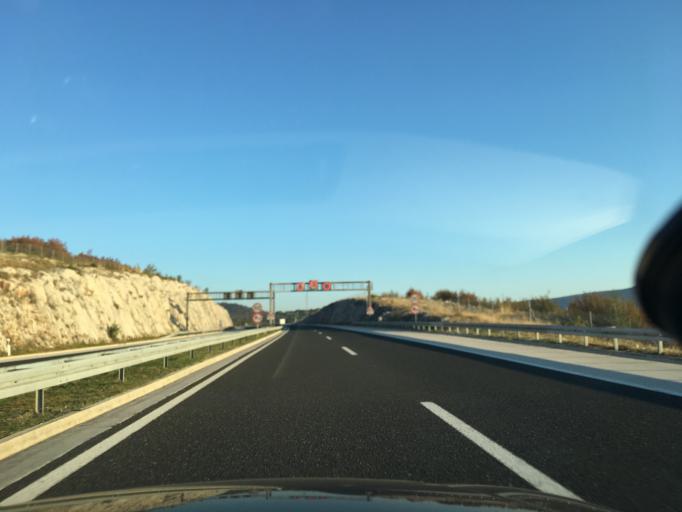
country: HR
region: Splitsko-Dalmatinska
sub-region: Grad Trogir
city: Trogir
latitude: 43.6488
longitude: 16.1994
